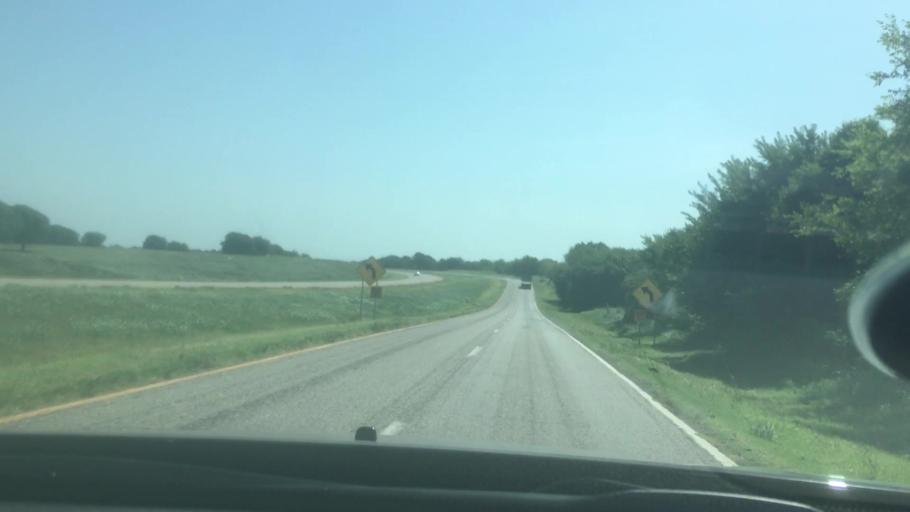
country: US
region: Oklahoma
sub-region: Pontotoc County
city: Ada
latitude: 34.6890
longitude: -96.7487
